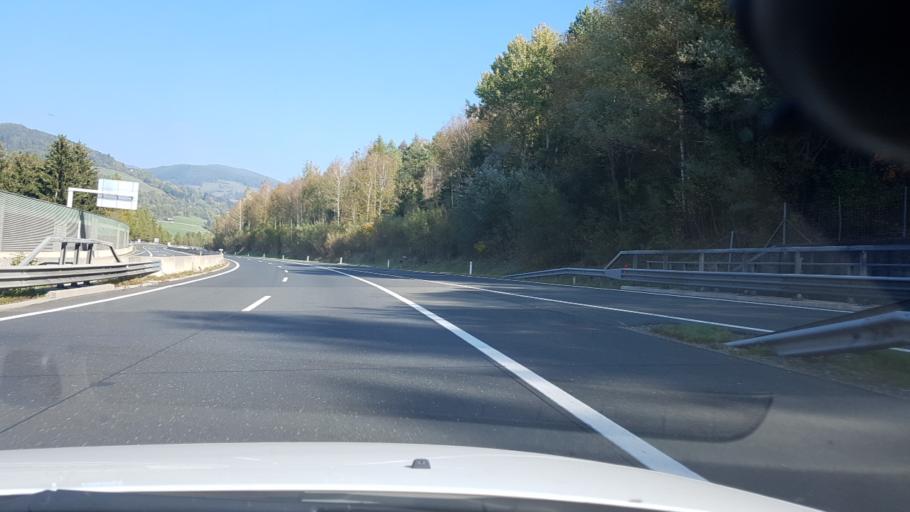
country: AT
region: Carinthia
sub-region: Politischer Bezirk Spittal an der Drau
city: Gmuend
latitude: 46.9016
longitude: 13.5415
